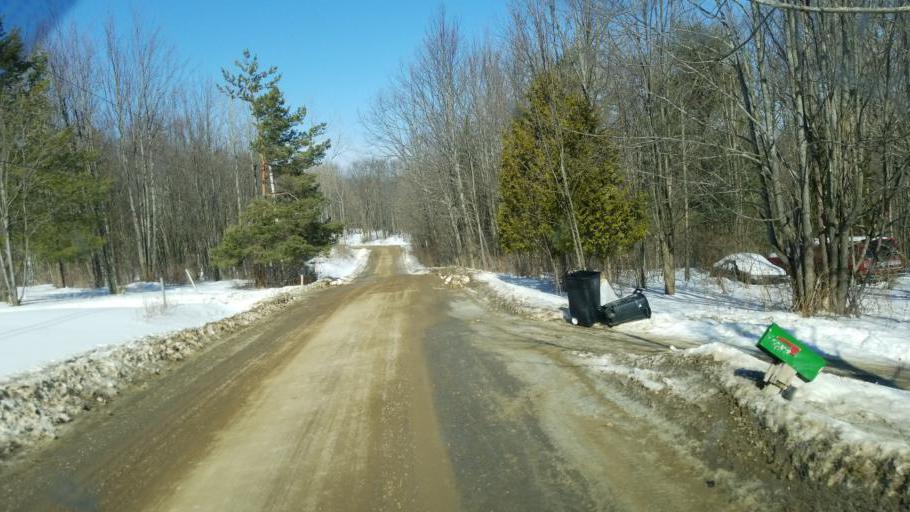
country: US
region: New York
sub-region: Allegany County
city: Alfred
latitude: 42.2670
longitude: -77.7162
